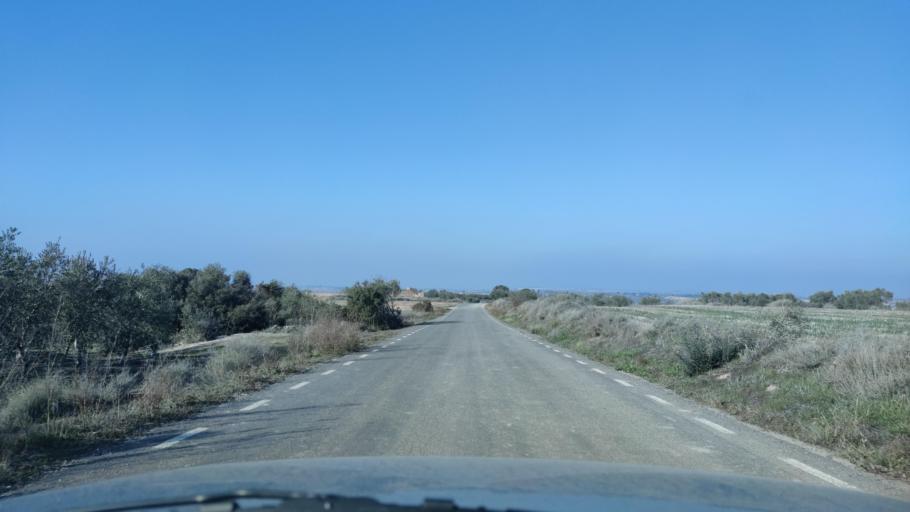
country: ES
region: Catalonia
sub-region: Provincia de Lleida
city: Torrebesses
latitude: 41.4490
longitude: 0.5586
